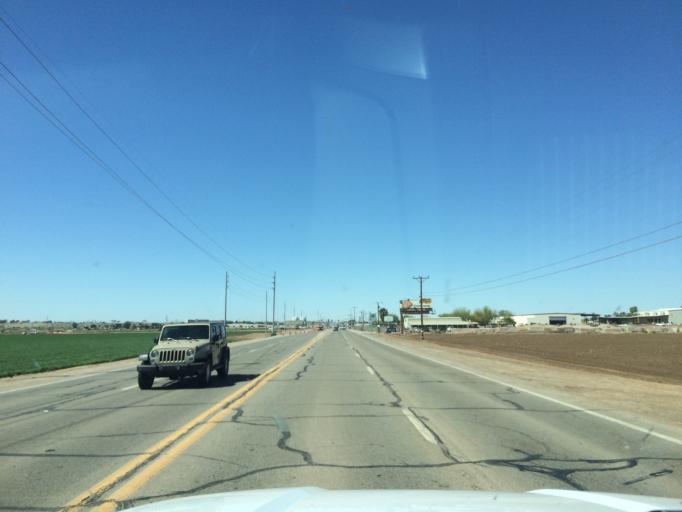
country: US
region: Arizona
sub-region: Yuma County
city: Yuma
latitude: 32.6988
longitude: -114.5772
